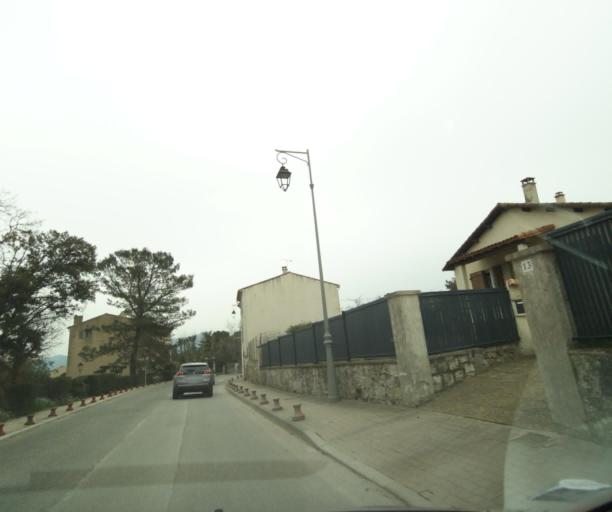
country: FR
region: Provence-Alpes-Cote d'Azur
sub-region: Departement des Bouches-du-Rhone
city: Peynier
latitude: 43.4466
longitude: 5.6408
